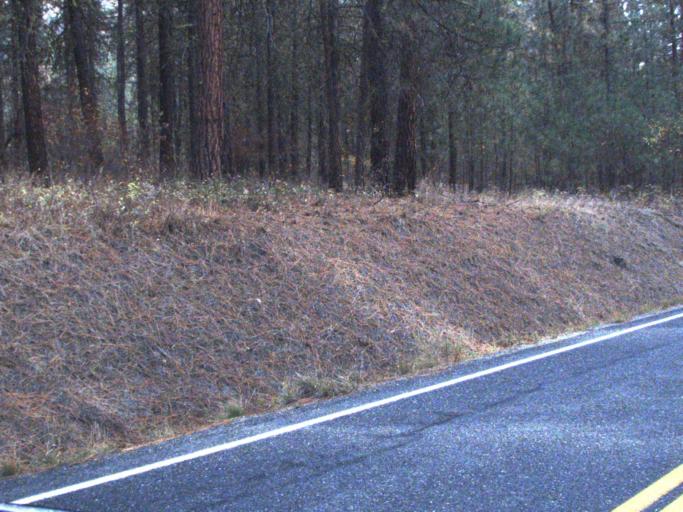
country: US
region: Washington
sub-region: Stevens County
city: Kettle Falls
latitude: 48.3001
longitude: -118.1473
